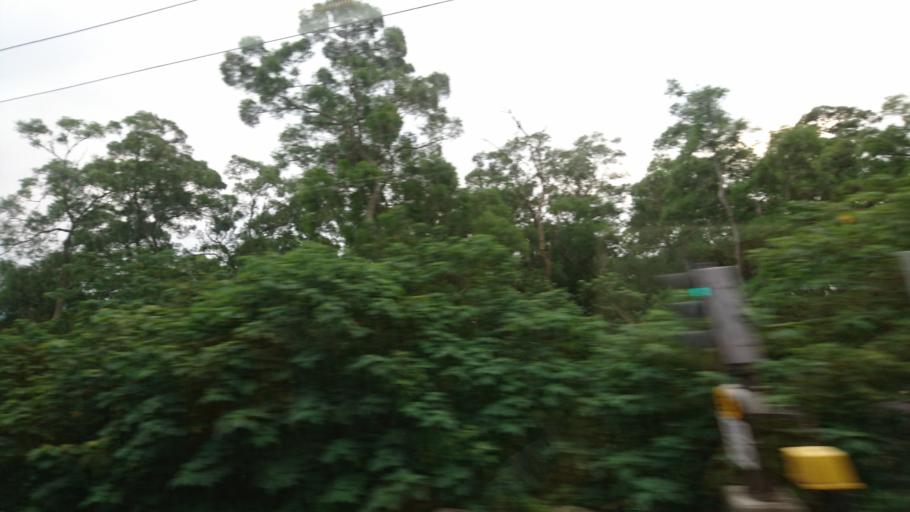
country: TW
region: Taiwan
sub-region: Hsinchu
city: Zhubei
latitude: 24.8592
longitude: 120.9989
